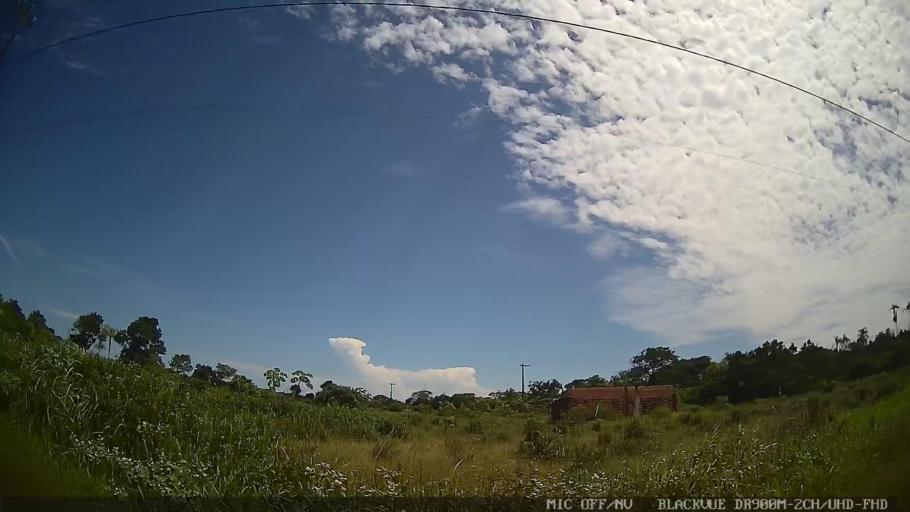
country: BR
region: Sao Paulo
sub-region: Iguape
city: Iguape
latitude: -24.7131
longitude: -47.5083
